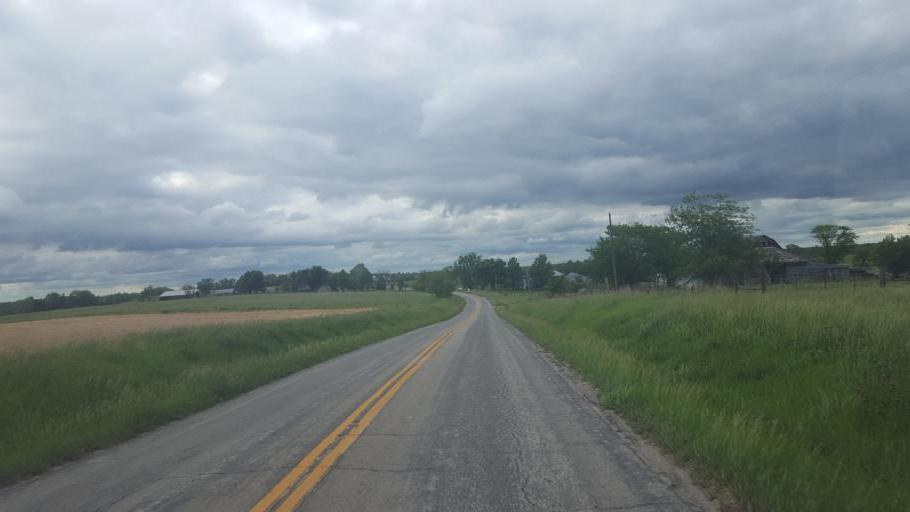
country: US
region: Missouri
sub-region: Mercer County
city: Princeton
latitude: 40.2746
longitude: -93.6757
